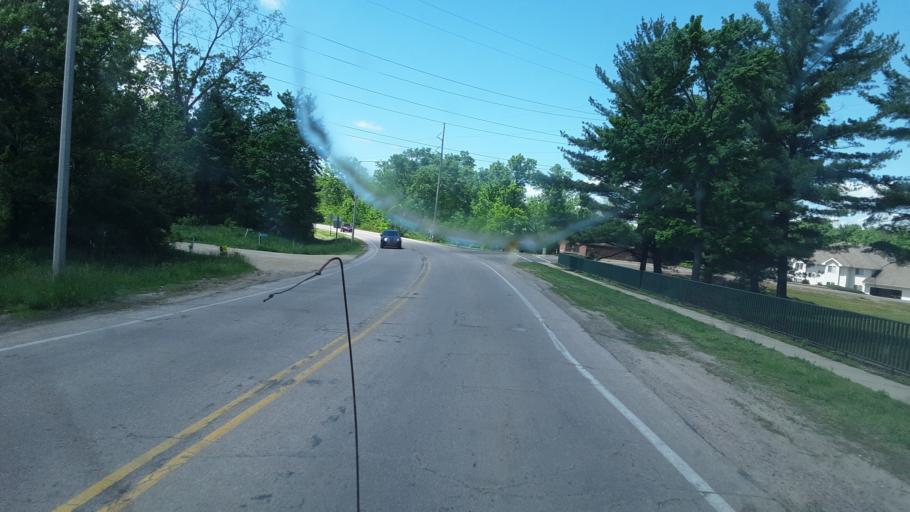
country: US
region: Wisconsin
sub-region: Sauk County
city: Lake Delton
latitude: 43.5889
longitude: -89.8149
